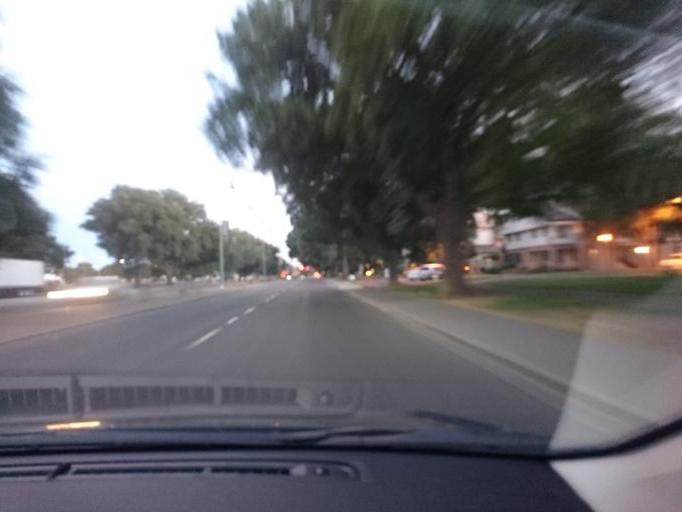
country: US
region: California
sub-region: Yolo County
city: Davis
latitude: 38.5422
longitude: -121.7609
